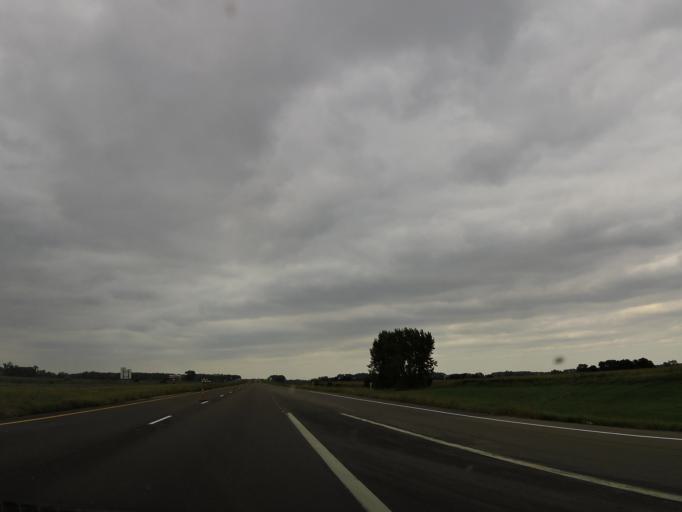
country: US
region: North Dakota
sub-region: Richland County
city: Wahpeton
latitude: 46.0545
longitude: -96.8353
